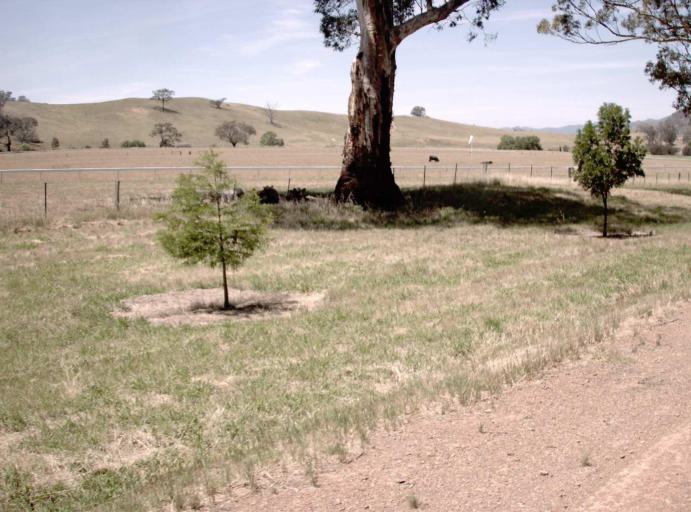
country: AU
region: Victoria
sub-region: East Gippsland
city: Bairnsdale
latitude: -37.2442
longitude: 147.7130
